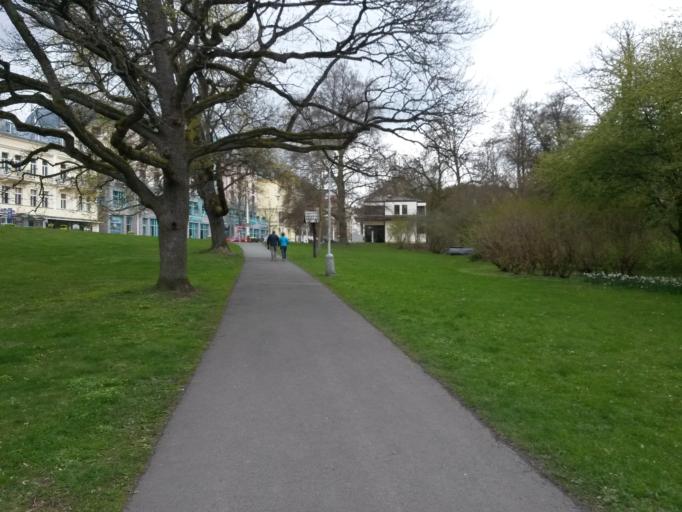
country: CZ
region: Karlovarsky
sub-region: Okres Cheb
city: Marianske Lazne
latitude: 49.9695
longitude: 12.7032
